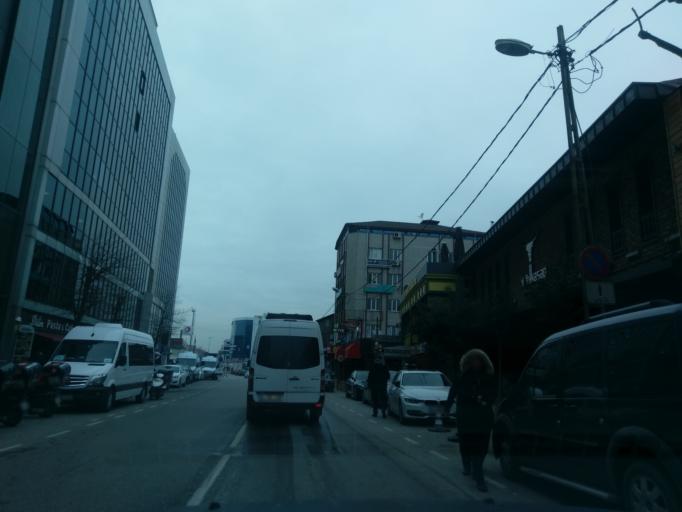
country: TR
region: Istanbul
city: Umraniye
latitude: 41.0949
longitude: 29.0989
